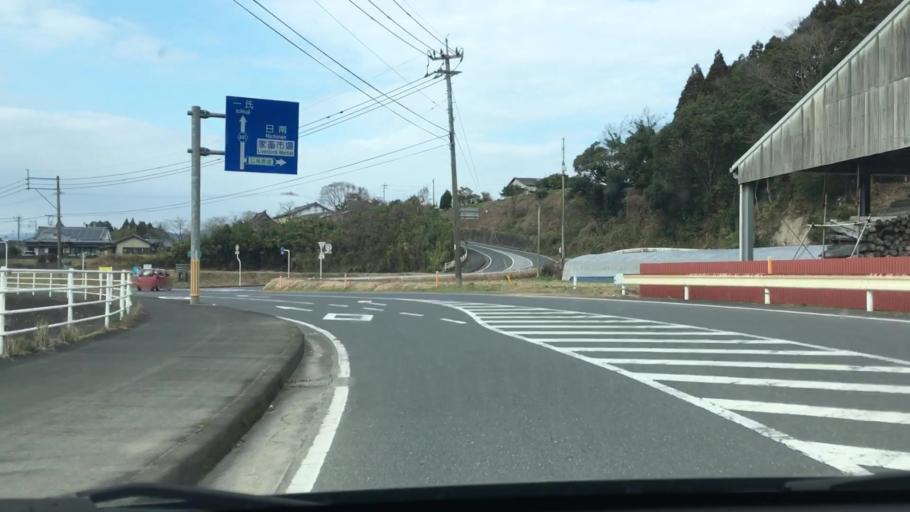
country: JP
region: Miyazaki
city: Kushima
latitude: 31.5003
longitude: 131.2389
